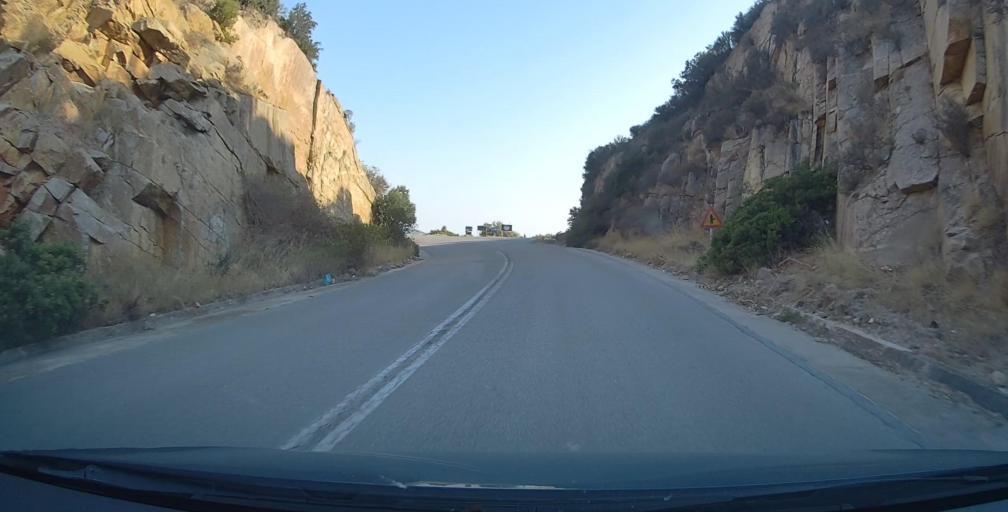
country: GR
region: Central Macedonia
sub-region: Nomos Chalkidikis
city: Sykia
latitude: 39.9998
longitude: 23.8883
